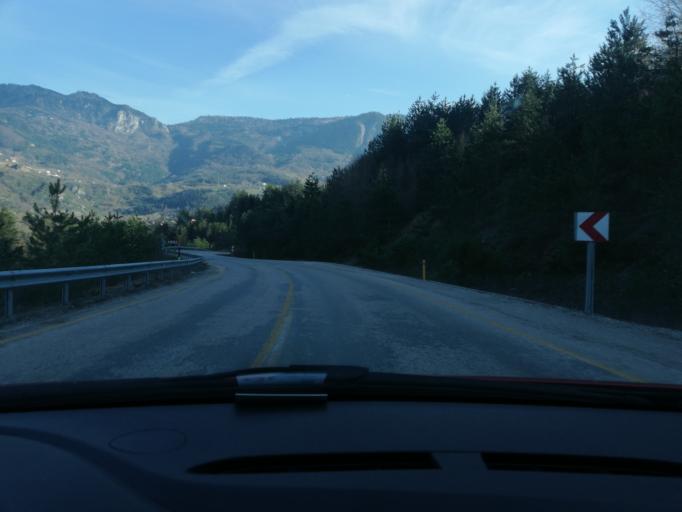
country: TR
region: Kastamonu
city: Senpazar
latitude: 41.7876
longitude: 33.1721
